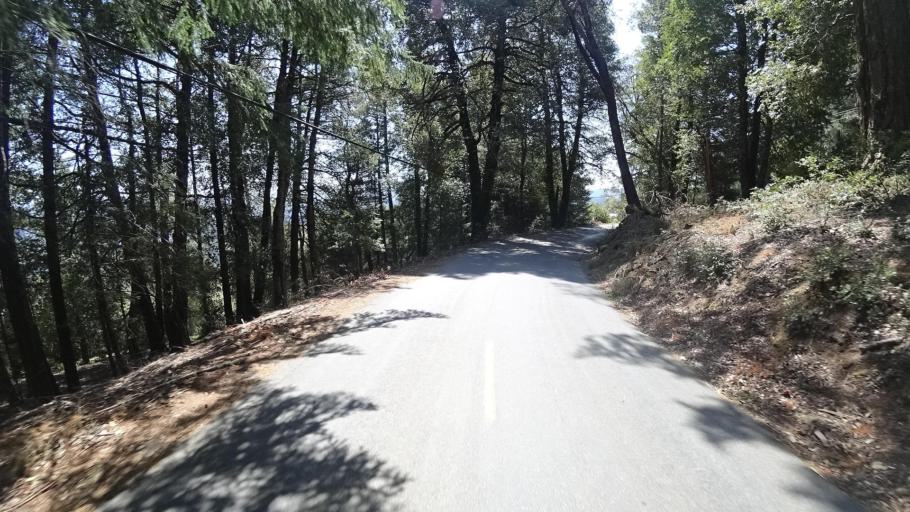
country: US
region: California
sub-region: Humboldt County
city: Redway
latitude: 40.0931
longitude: -123.6773
